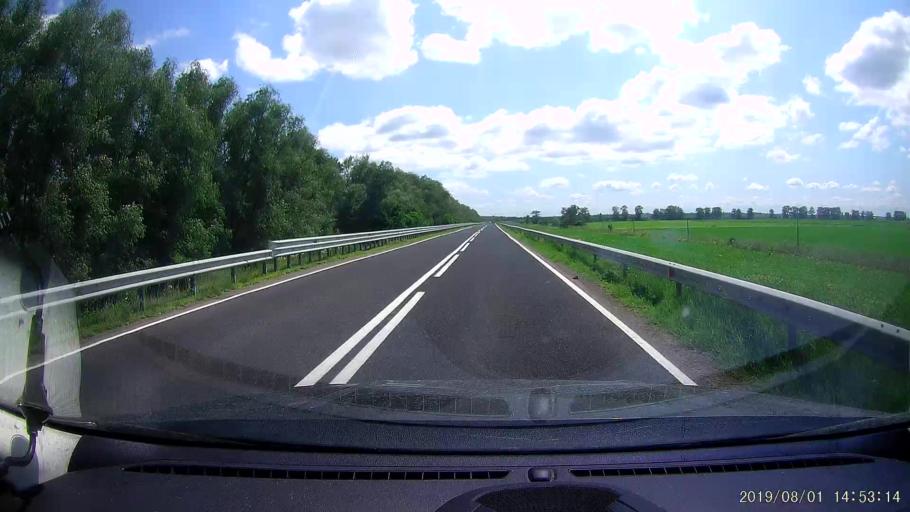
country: RO
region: Braila
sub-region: Municipiul Braila
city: Braila
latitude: 45.3399
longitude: 28.0054
